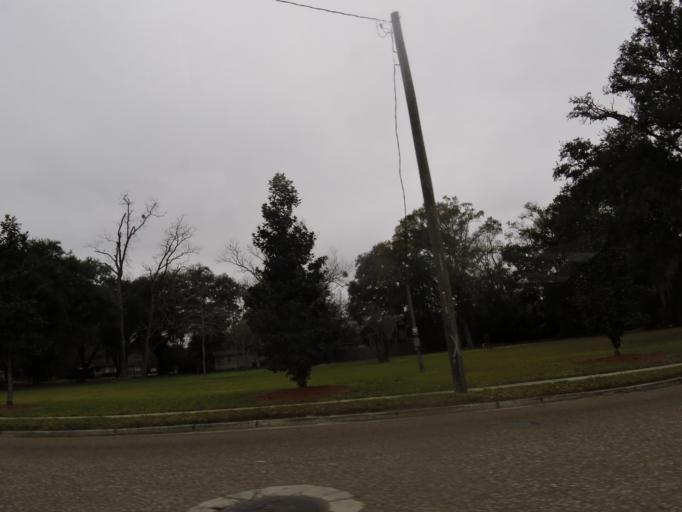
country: US
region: Florida
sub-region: Duval County
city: Jacksonville
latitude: 30.3664
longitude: -81.6989
